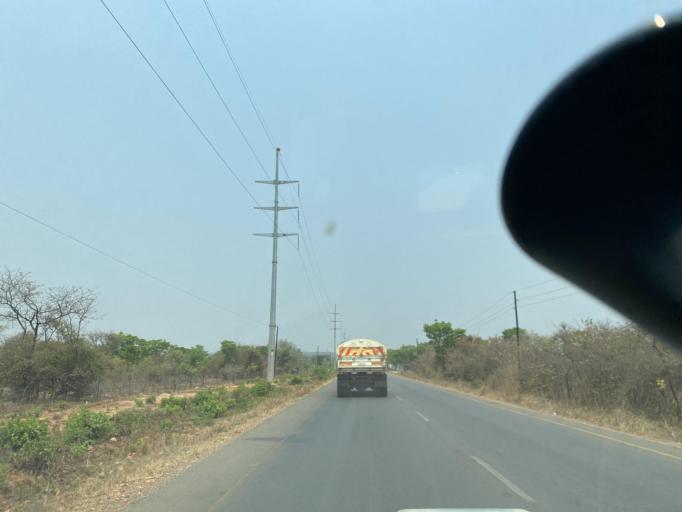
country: ZM
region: Lusaka
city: Lusaka
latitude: -15.5179
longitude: 28.4556
